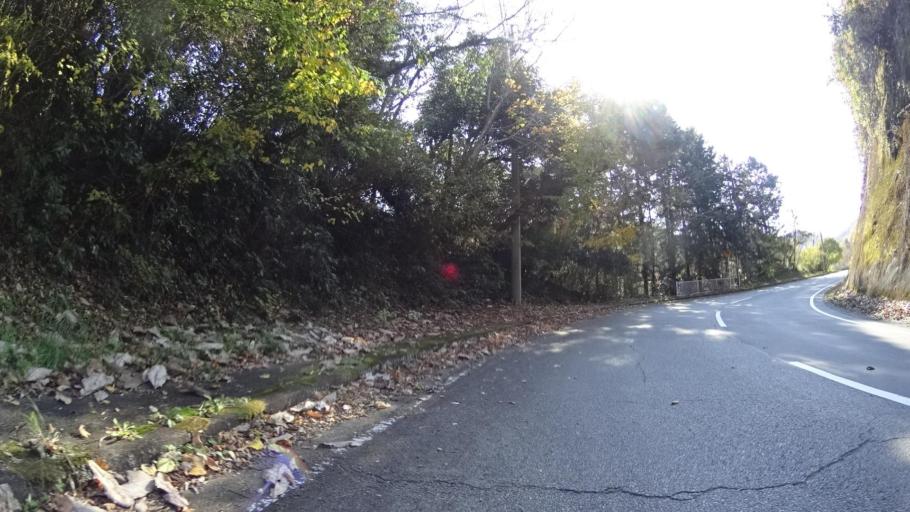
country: JP
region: Yamanashi
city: Uenohara
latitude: 35.5897
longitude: 139.1676
